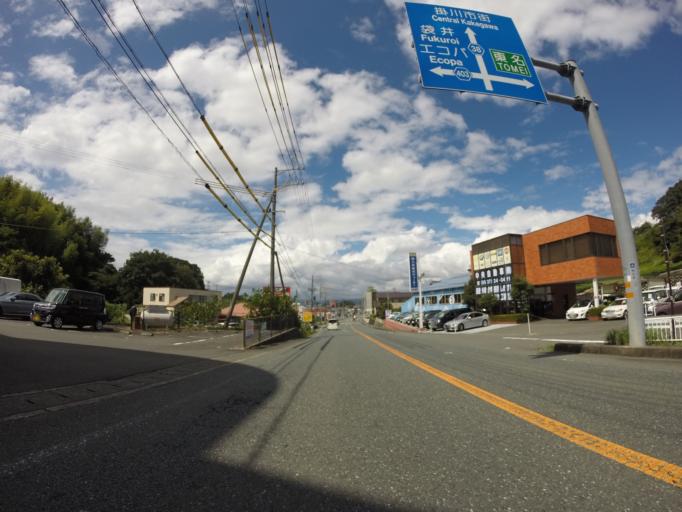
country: JP
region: Shizuoka
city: Kakegawa
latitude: 34.7602
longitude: 138.0226
